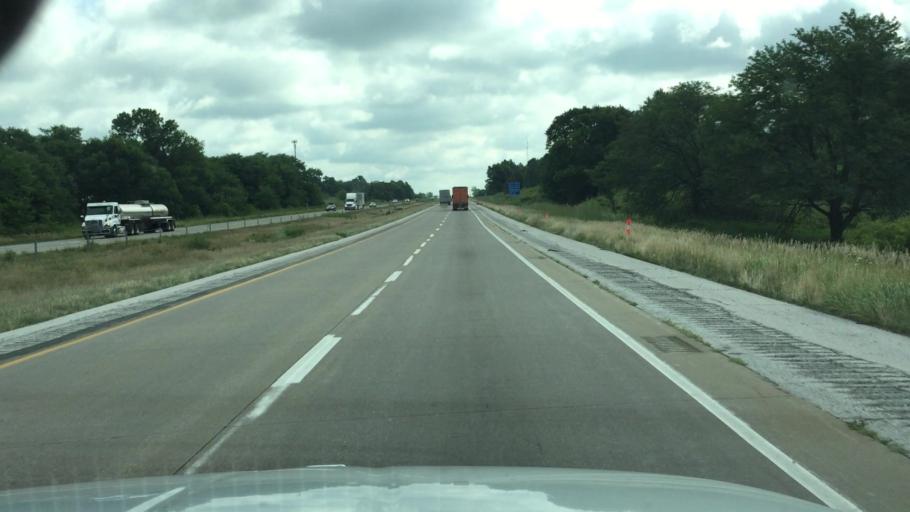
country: US
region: Iowa
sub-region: Scott County
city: Bettendorf
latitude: 41.5962
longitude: -90.5064
